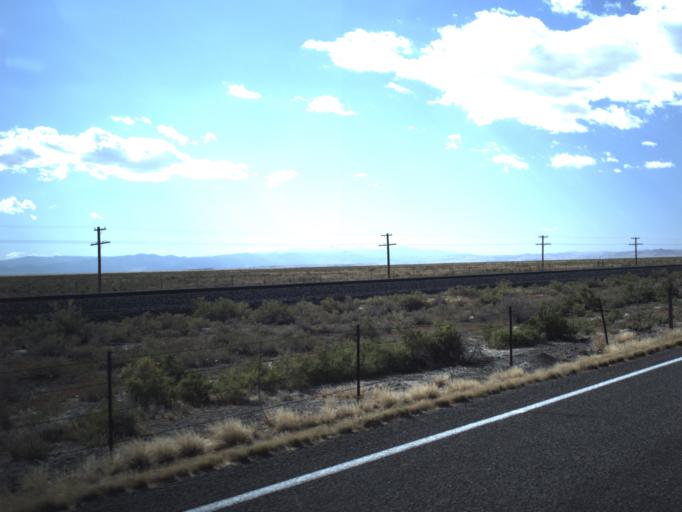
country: US
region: Utah
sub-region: Millard County
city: Delta
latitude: 39.1022
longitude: -112.7468
